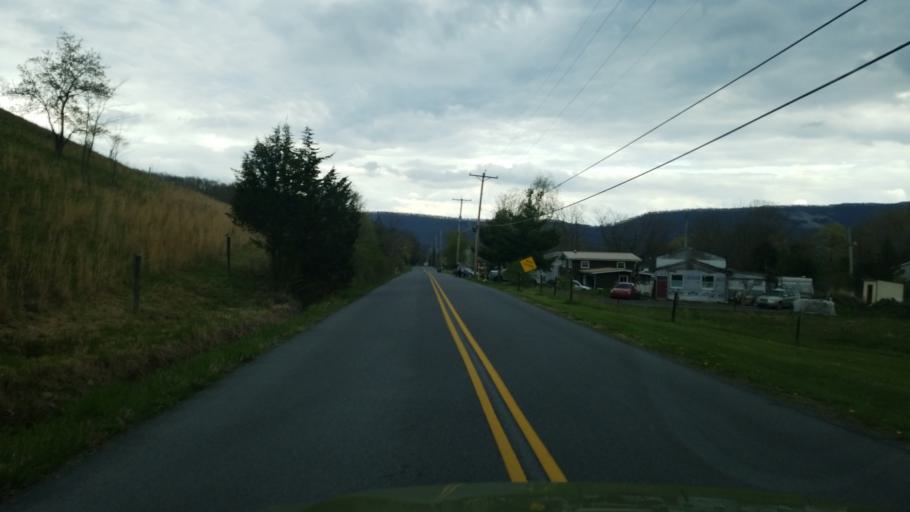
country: US
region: Pennsylvania
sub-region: Blair County
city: Tipton
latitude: 40.6456
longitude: -78.3144
